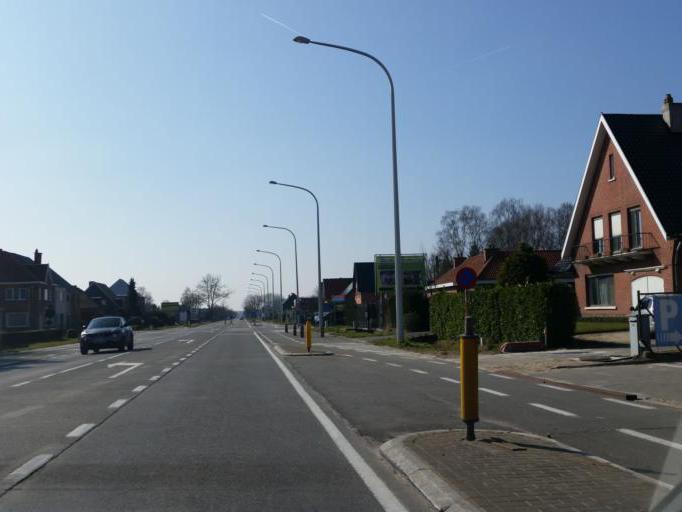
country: BE
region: Flanders
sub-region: Provincie Oost-Vlaanderen
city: Waasmunster
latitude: 51.1298
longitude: 4.0473
